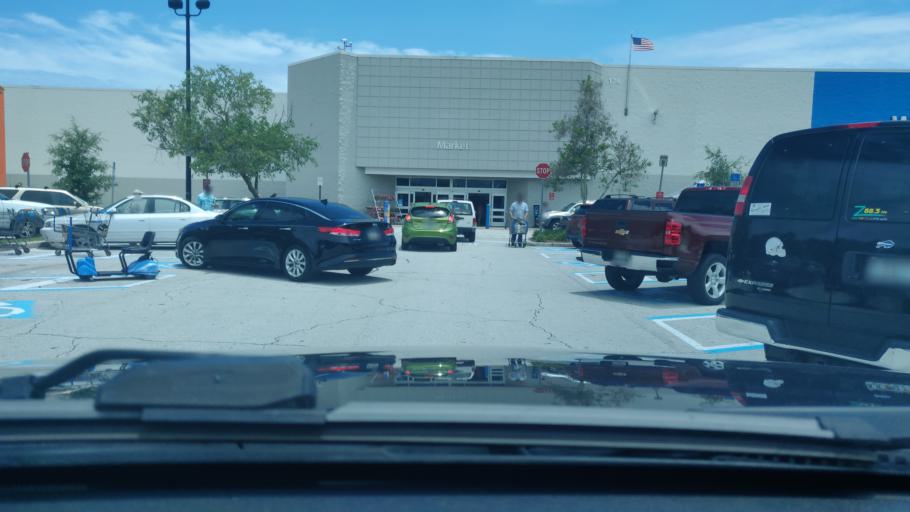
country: US
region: Florida
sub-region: Flagler County
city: Palm Coast
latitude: 29.5507
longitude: -81.2253
